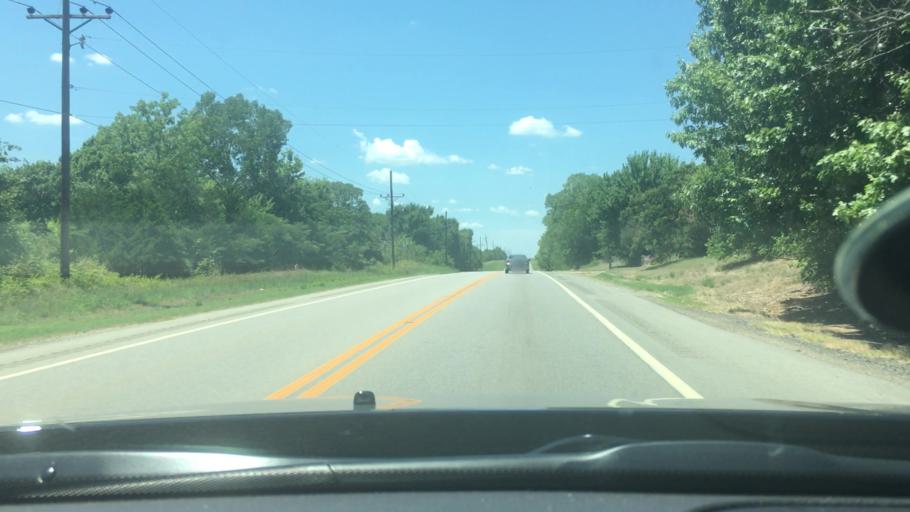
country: US
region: Oklahoma
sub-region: Bryan County
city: Durant
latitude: 34.0036
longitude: -96.2002
